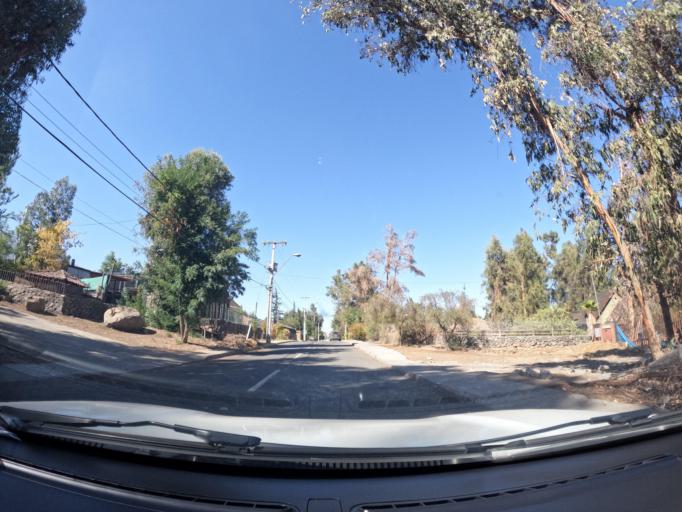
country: CL
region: Santiago Metropolitan
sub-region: Provincia de Santiago
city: Villa Presidente Frei, Nunoa, Santiago, Chile
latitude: -33.4950
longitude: -70.5328
